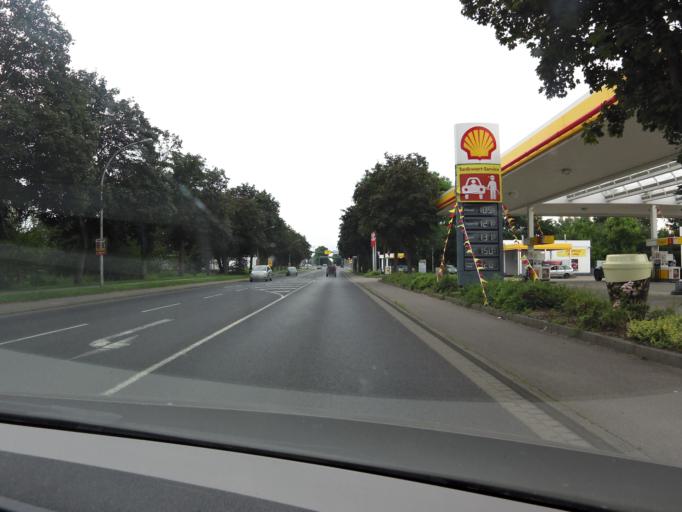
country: DE
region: Mecklenburg-Vorpommern
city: Neustrelitz
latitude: 53.3467
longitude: 13.0814
